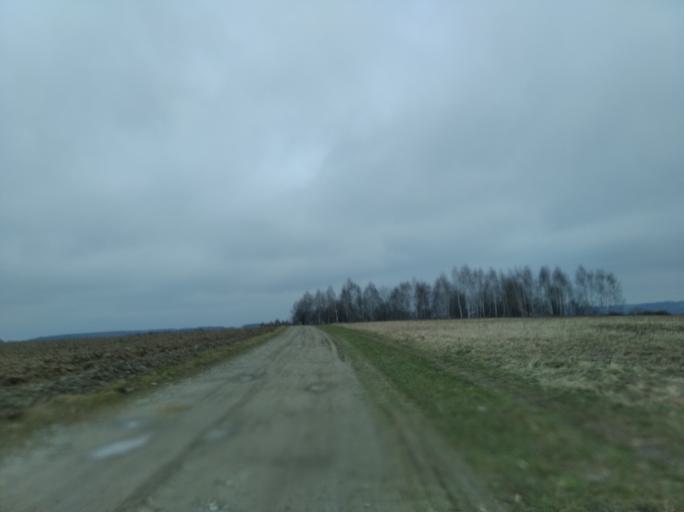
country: PL
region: Subcarpathian Voivodeship
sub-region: Powiat strzyzowski
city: Strzyzow
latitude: 49.8834
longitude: 21.8014
